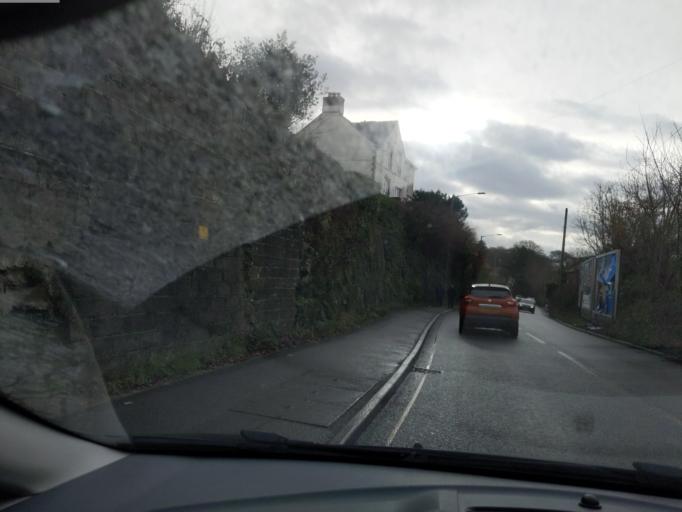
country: GB
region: England
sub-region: Cornwall
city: Launceston
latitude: 50.6353
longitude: -4.3645
